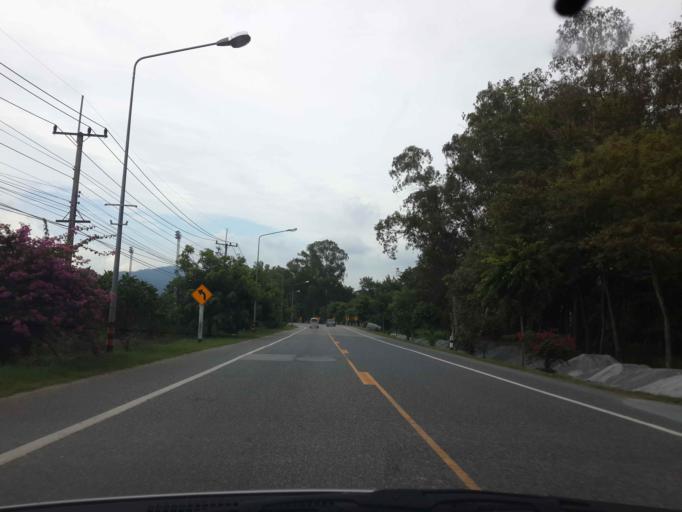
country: TH
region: Chon Buri
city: Si Racha
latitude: 13.2335
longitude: 100.9826
